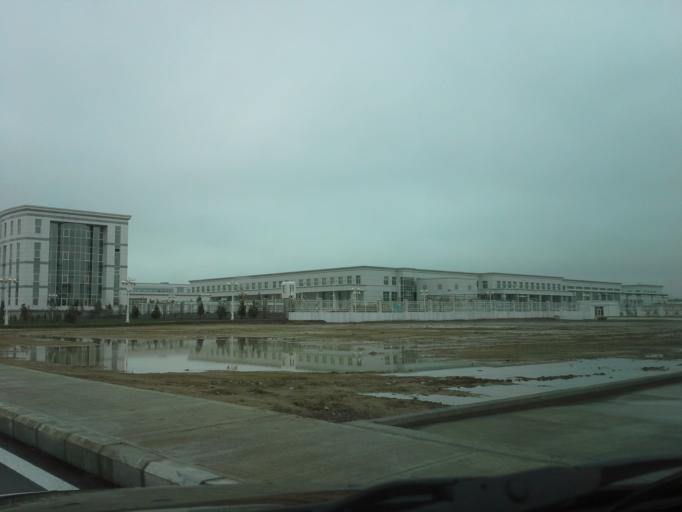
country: TM
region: Ahal
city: Ashgabat
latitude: 37.9667
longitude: 58.4088
